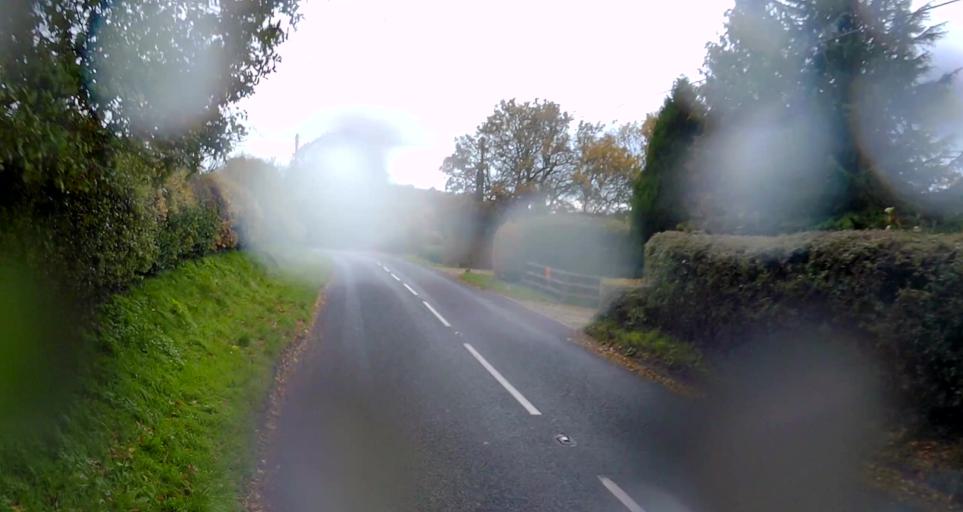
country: GB
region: England
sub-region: Hampshire
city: Kings Worthy
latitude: 51.1303
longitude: -1.1888
